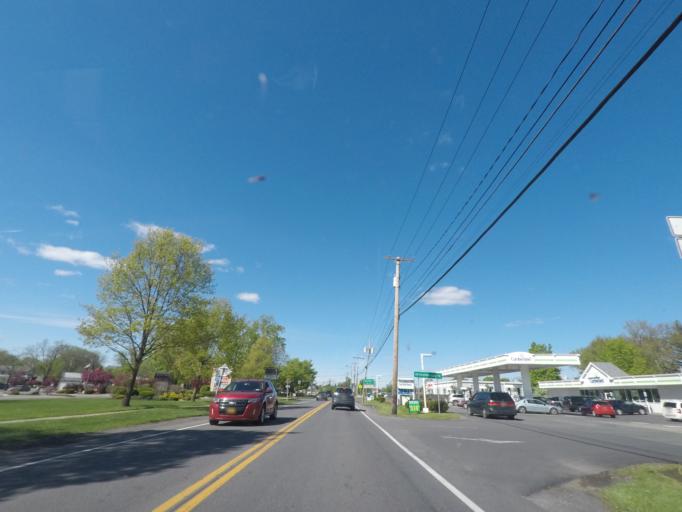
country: US
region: New York
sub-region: Albany County
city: Delmar
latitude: 42.6002
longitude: -73.7929
